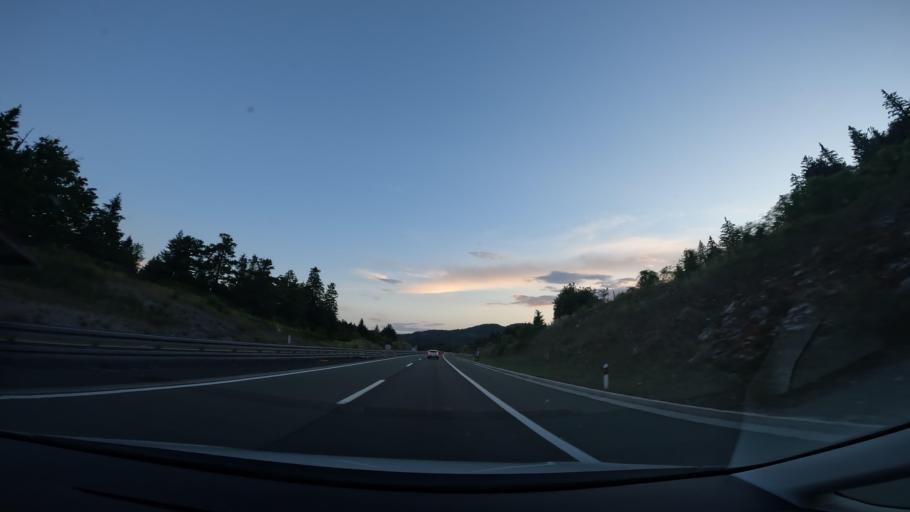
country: HR
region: Primorsko-Goranska
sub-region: Grad Delnice
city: Delnice
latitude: 45.3674
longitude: 14.7608
